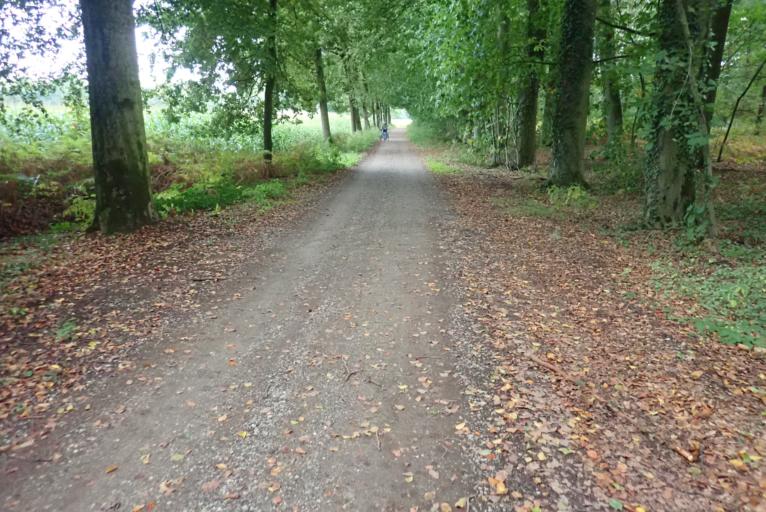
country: BE
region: Flanders
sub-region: Provincie Antwerpen
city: Vorselaar
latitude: 51.1991
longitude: 4.7539
